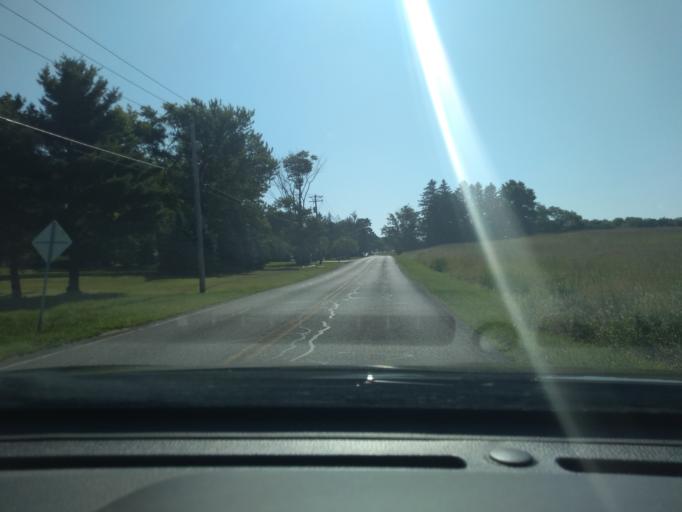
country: US
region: New York
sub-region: Erie County
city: Billington Heights
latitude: 42.7776
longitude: -78.6542
